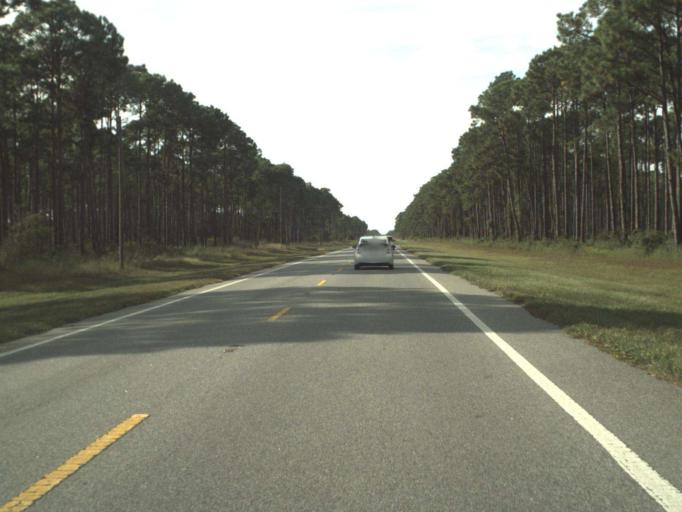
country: US
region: Florida
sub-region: Bay County
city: Mexico Beach
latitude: 30.0088
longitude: -85.5108
